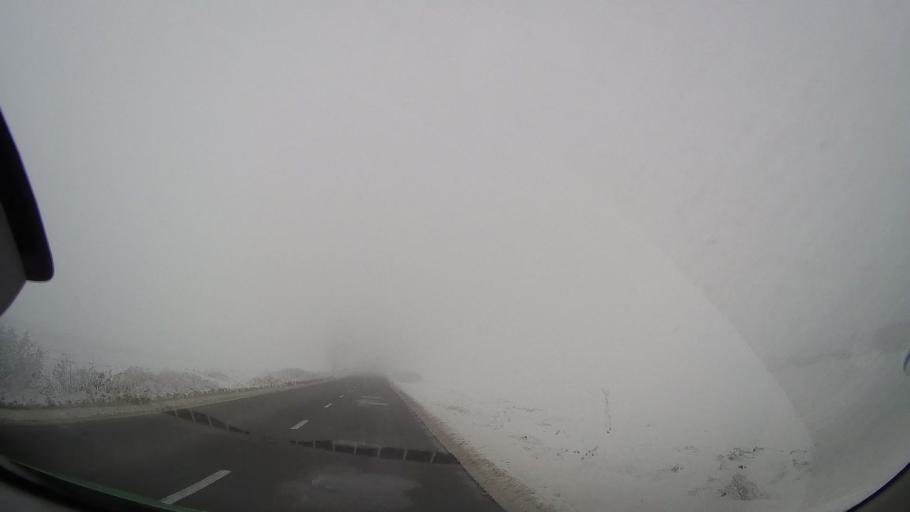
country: RO
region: Neamt
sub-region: Comuna Sabaoani
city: Sabaoani
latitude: 47.0383
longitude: 26.8530
